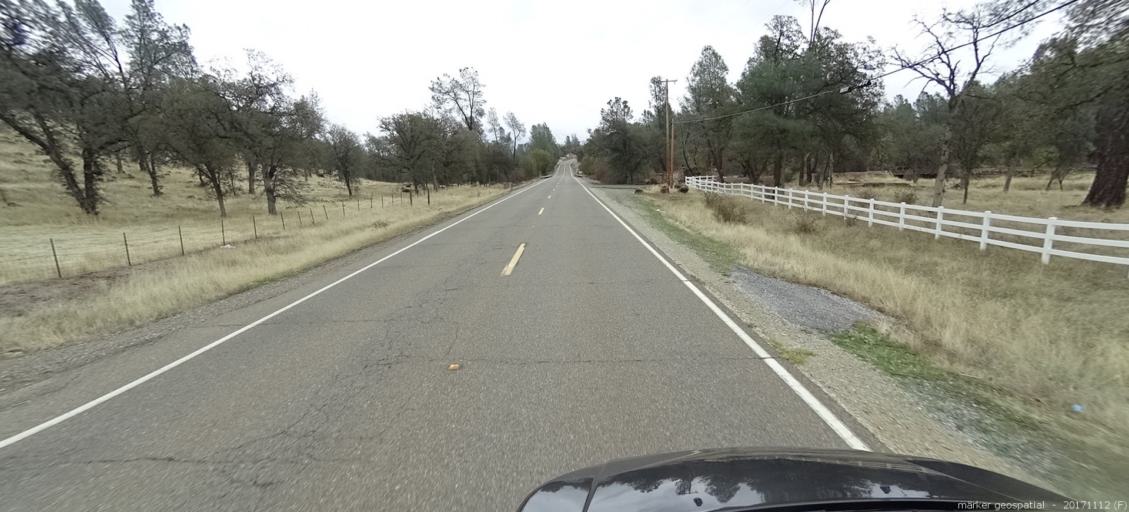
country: US
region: California
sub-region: Shasta County
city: Palo Cedro
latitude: 40.4879
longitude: -122.1372
